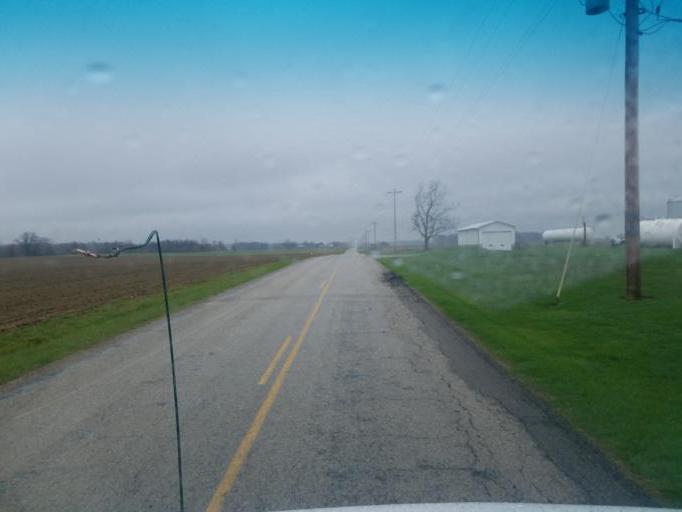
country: US
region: Ohio
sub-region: Crawford County
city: Bucyrus
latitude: 40.9649
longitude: -82.9816
